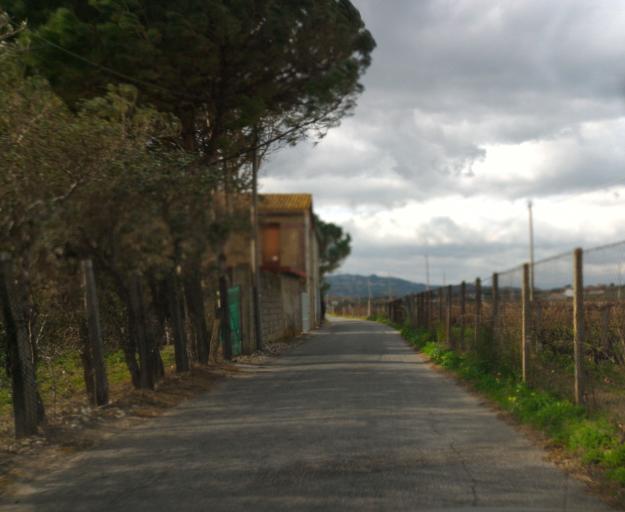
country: IT
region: Calabria
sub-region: Provincia di Crotone
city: Ciro Marina
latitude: 39.3906
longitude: 17.1318
